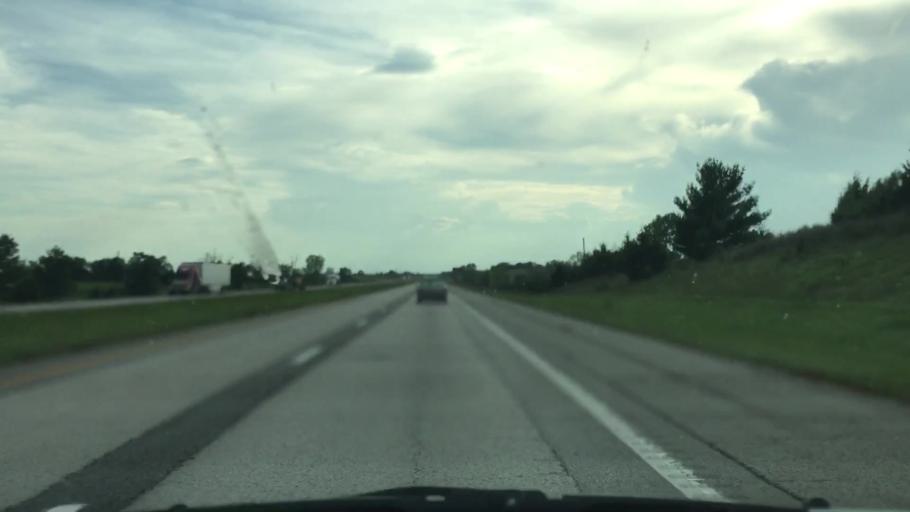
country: US
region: Missouri
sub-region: Harrison County
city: Bethany
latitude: 40.1645
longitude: -94.0263
